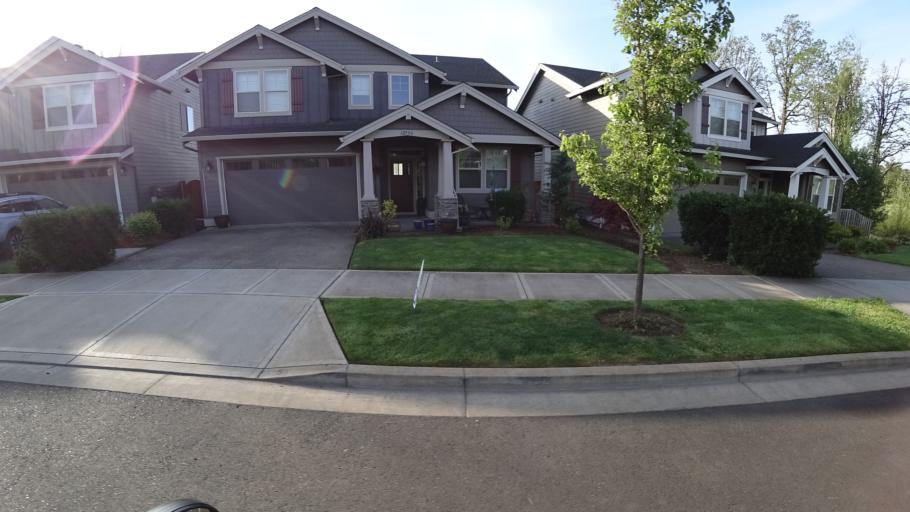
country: US
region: Oregon
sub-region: Washington County
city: King City
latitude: 45.4283
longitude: -122.8487
